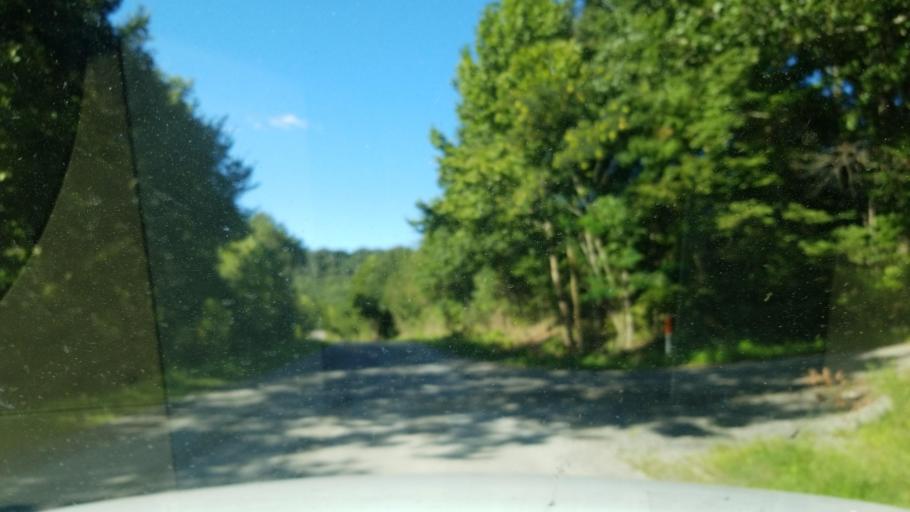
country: US
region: Illinois
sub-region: Hardin County
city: Elizabethtown
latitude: 37.5920
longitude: -88.3654
